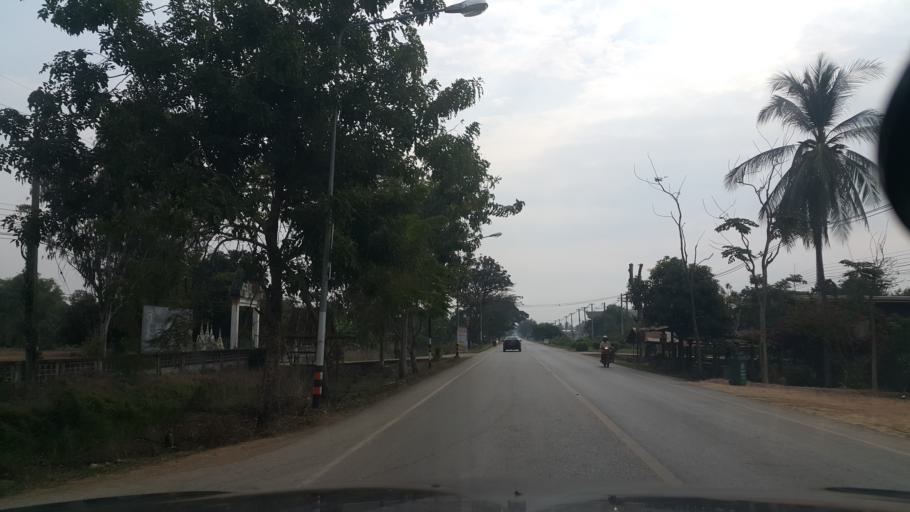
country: TH
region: Sukhothai
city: Si Samrong
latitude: 17.1820
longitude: 99.8341
